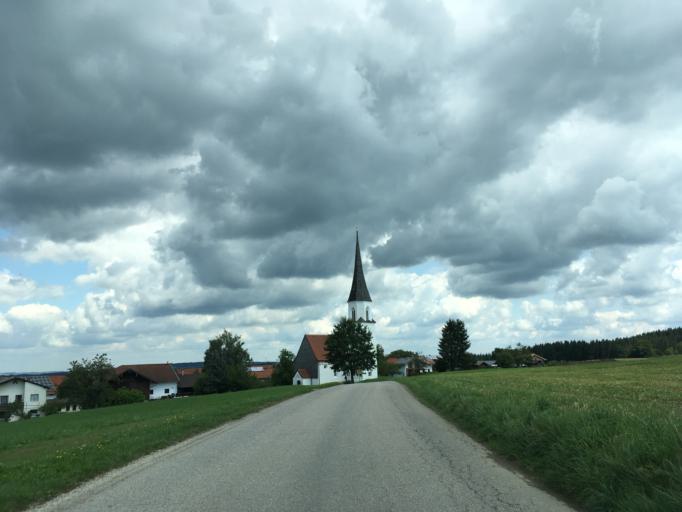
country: DE
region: Bavaria
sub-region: Upper Bavaria
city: Amerang
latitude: 48.0073
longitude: 12.3473
